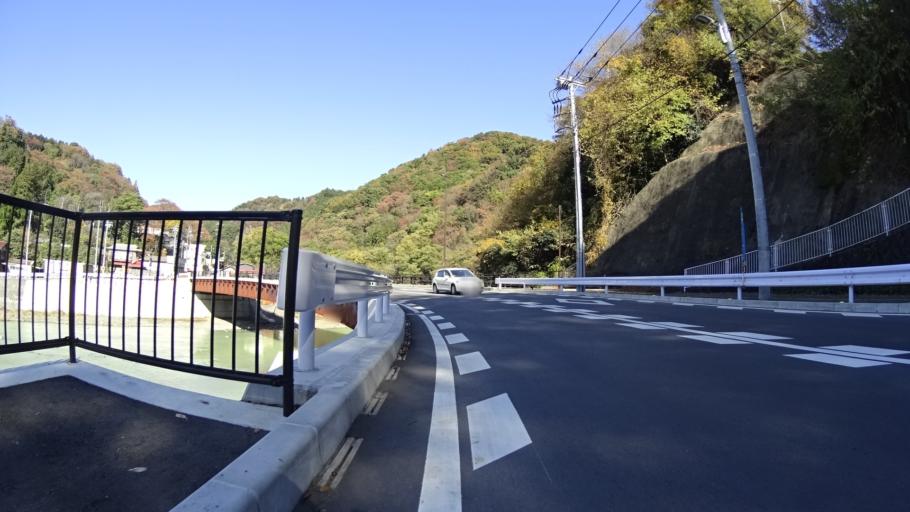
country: JP
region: Kanagawa
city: Zama
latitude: 35.5313
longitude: 139.2854
